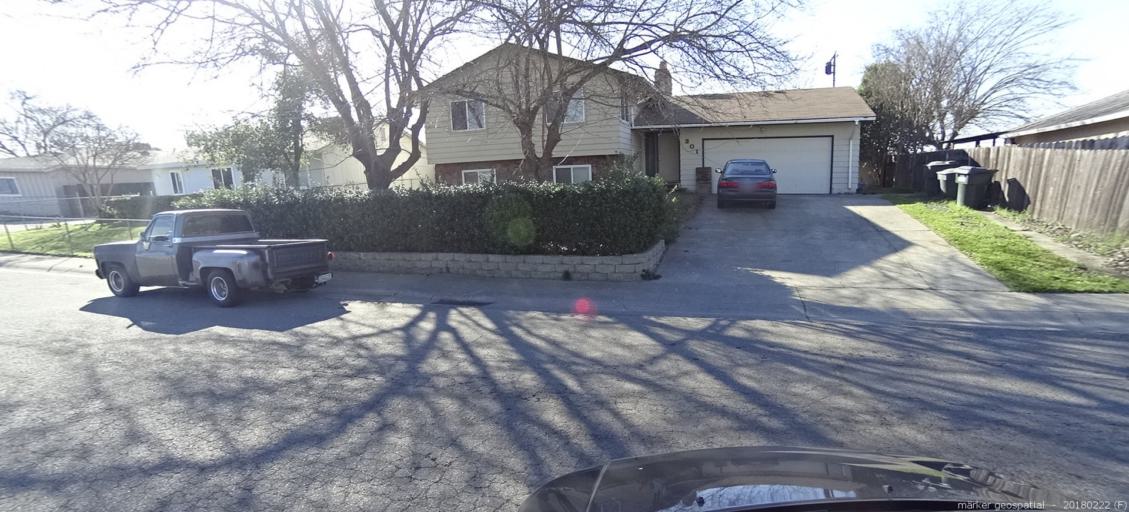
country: US
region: California
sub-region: Sacramento County
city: Elverta
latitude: 38.7223
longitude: -121.4686
